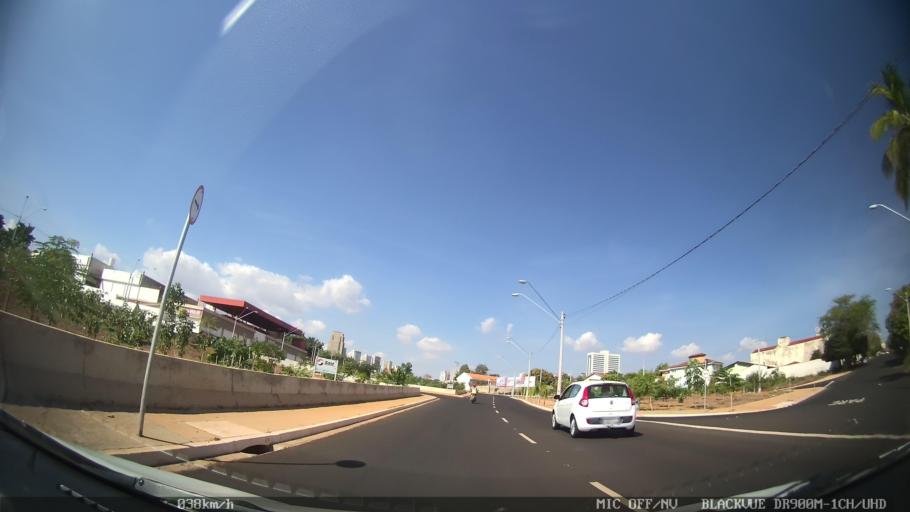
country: BR
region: Sao Paulo
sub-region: Ribeirao Preto
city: Ribeirao Preto
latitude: -21.2043
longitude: -47.8192
